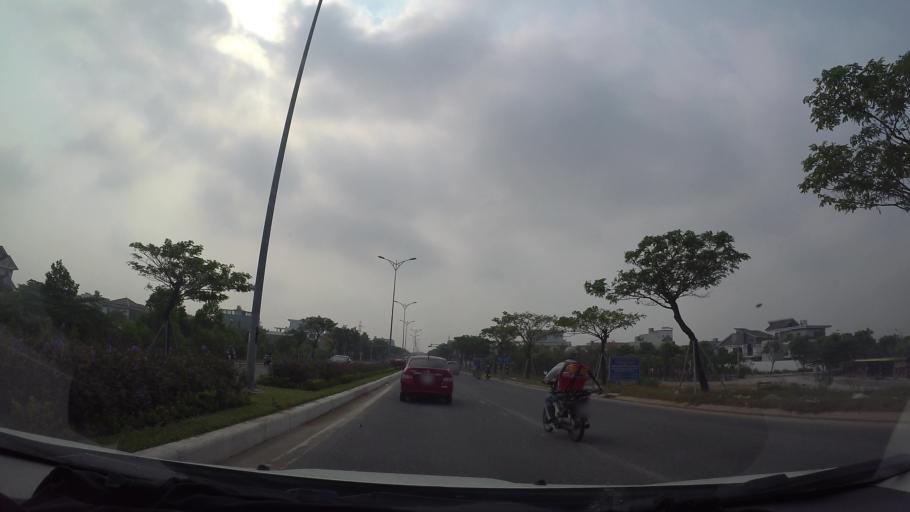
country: VN
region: Da Nang
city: Cam Le
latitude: 16.0118
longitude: 108.2164
